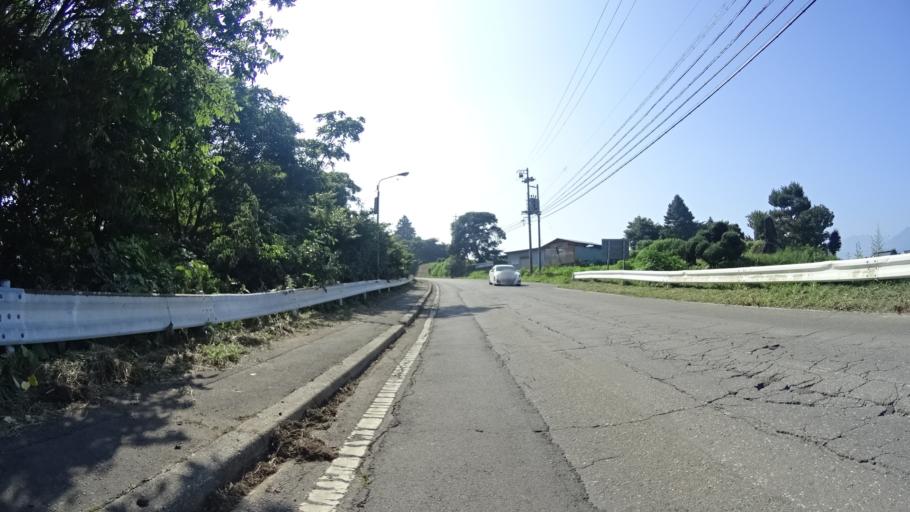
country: JP
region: Nagano
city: Chino
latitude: 35.9574
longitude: 138.2302
